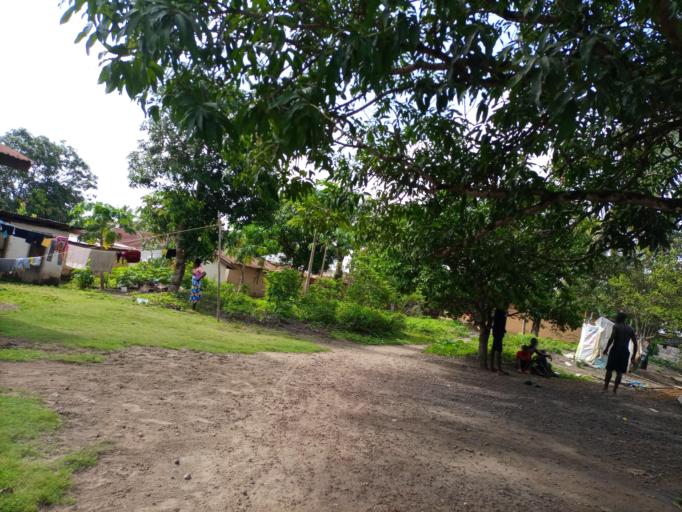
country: SL
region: Southern Province
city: Bo
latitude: 7.9654
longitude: -11.7612
